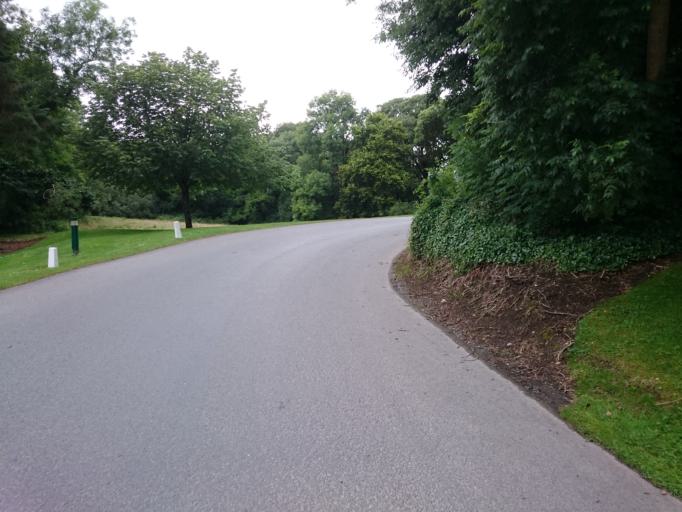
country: IE
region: Connaught
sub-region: Maigh Eo
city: Ballinrobe
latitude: 53.5380
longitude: -9.2859
